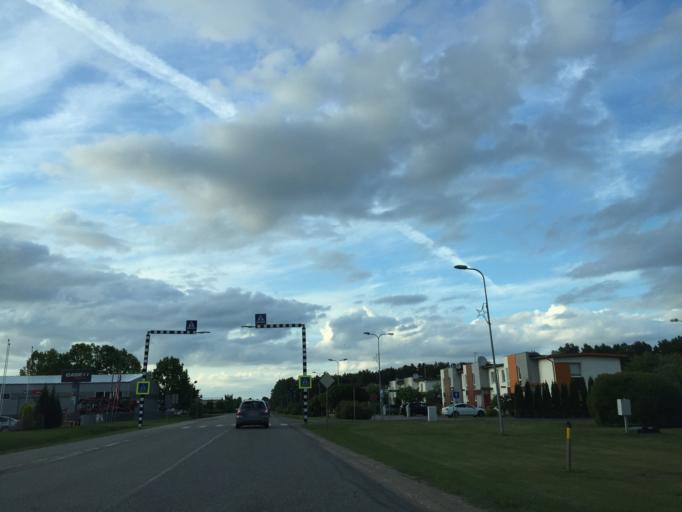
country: LV
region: Babite
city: Pinki
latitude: 56.9469
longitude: 23.9118
